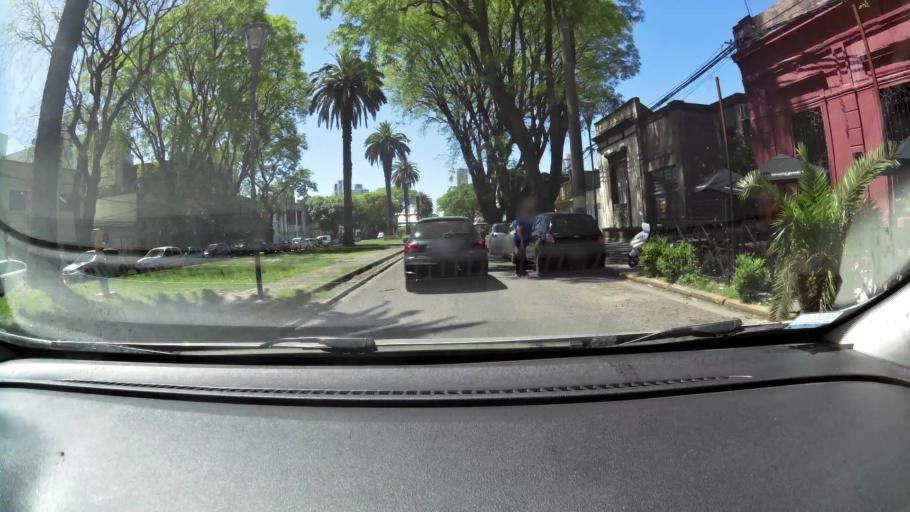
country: AR
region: Santa Fe
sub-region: Departamento de Rosario
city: Rosario
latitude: -32.9344
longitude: -60.6637
